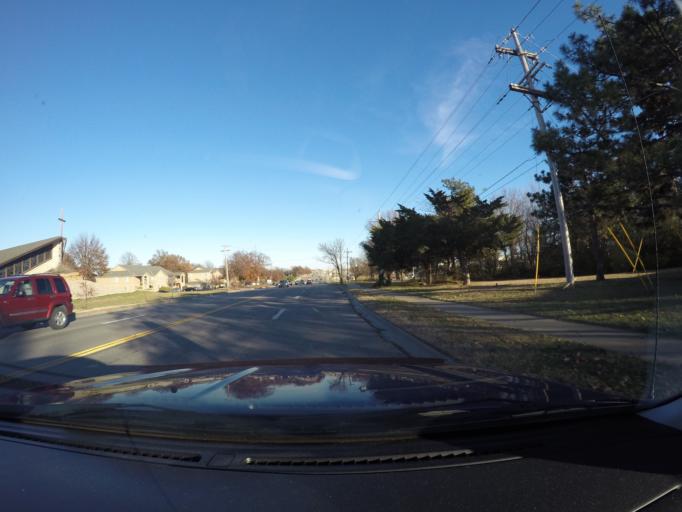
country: US
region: Kansas
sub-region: Riley County
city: Manhattan
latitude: 39.2038
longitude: -96.6014
